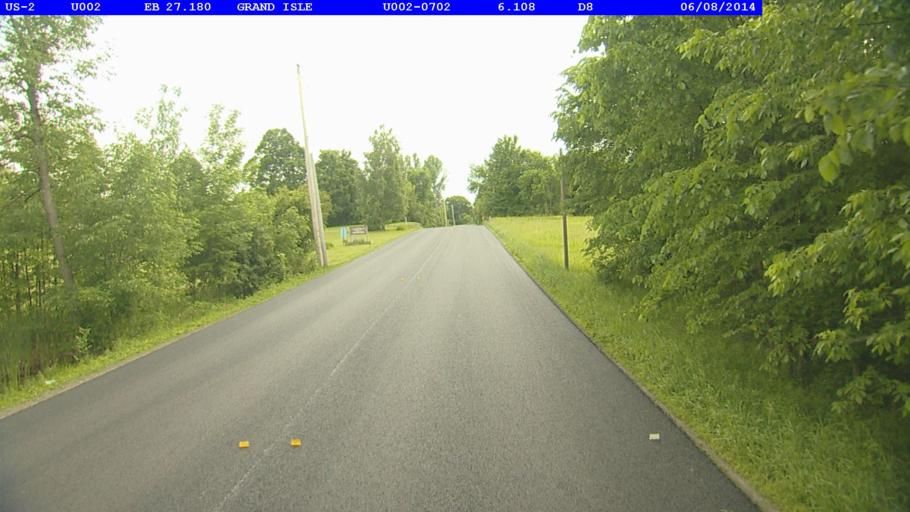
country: US
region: New York
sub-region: Clinton County
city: Cumberland Head
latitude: 44.6823
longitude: -73.3144
